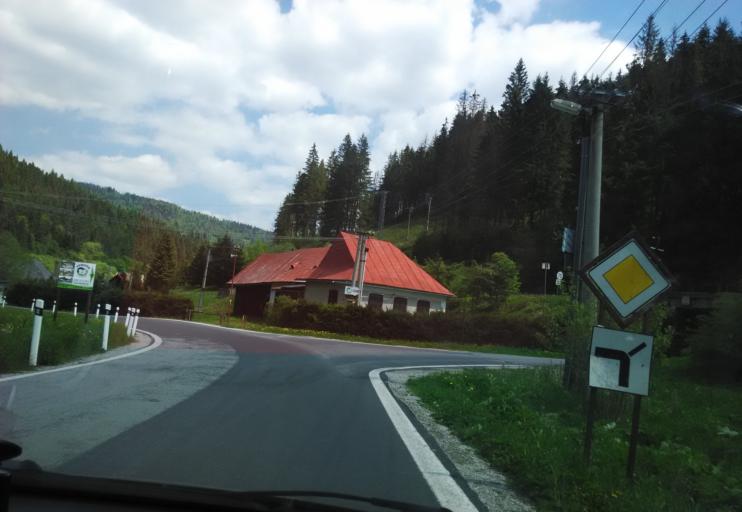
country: SK
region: Kosicky
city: Dobsina
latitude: 48.8555
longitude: 20.4140
